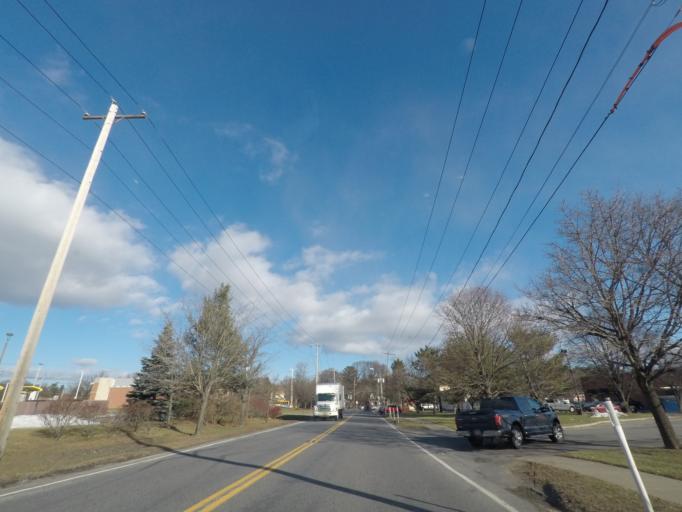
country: US
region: New York
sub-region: Albany County
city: Colonie
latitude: 42.7292
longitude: -73.8483
